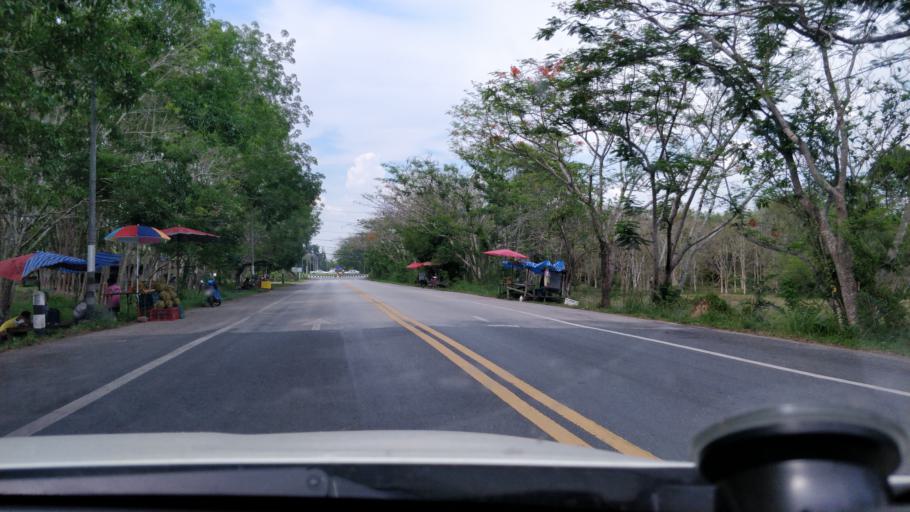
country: TH
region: Surat Thani
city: Ban Na Doem
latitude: 8.9350
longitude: 99.2633
